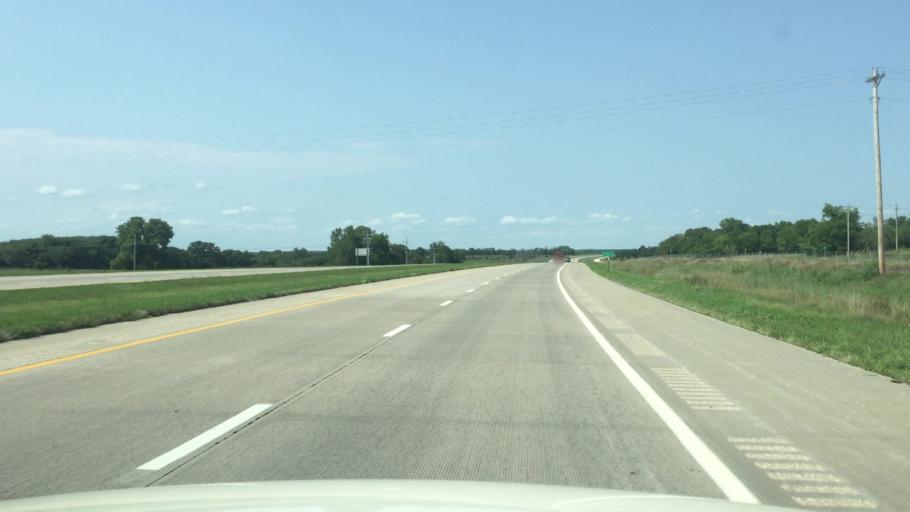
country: US
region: Kansas
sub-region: Linn County
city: Pleasanton
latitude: 38.1950
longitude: -94.7054
